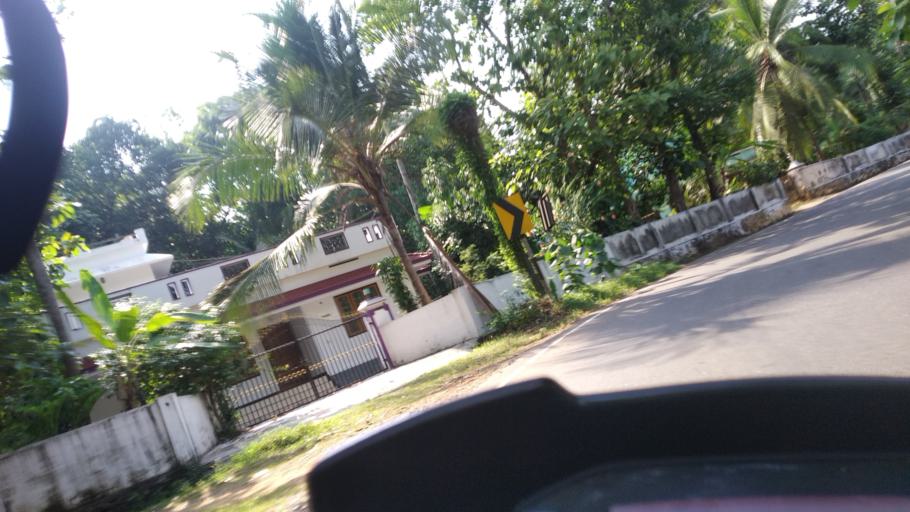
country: IN
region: Kerala
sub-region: Ernakulam
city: Piravam
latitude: 9.8380
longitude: 76.5378
